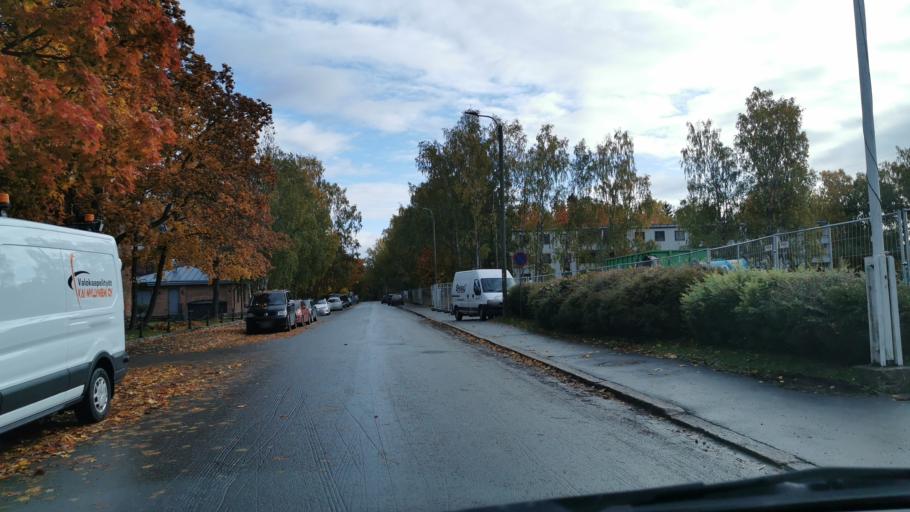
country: FI
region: Ostrobothnia
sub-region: Vaasa
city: Vaasa
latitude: 63.0923
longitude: 21.5594
